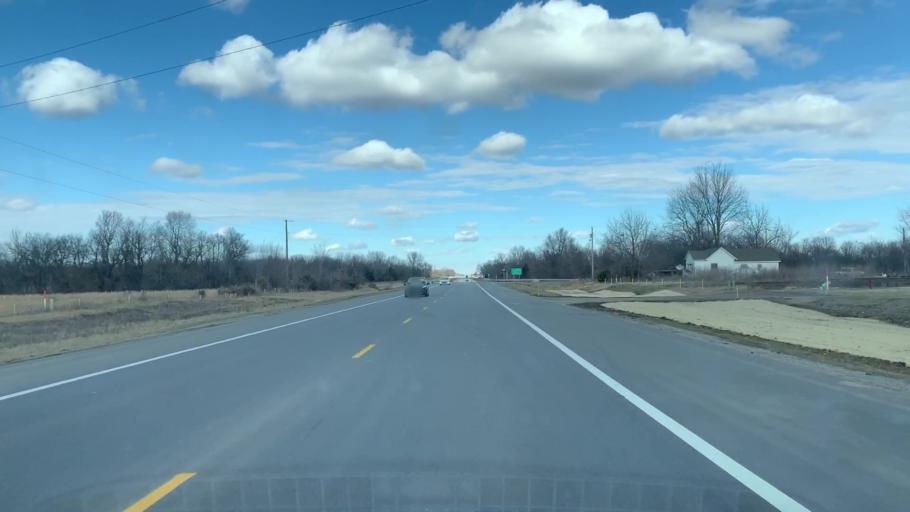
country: US
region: Kansas
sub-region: Cherokee County
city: Columbus
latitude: 37.2725
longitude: -94.8321
